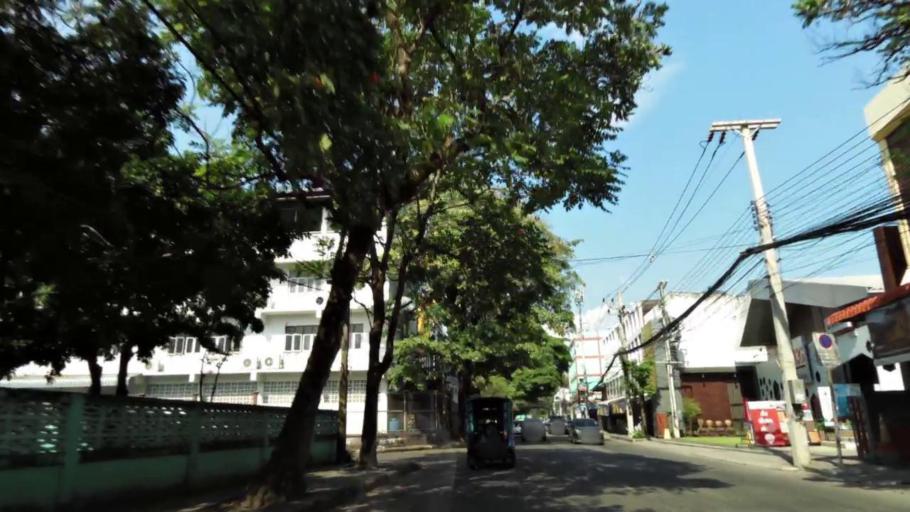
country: TH
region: Chiang Rai
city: Chiang Rai
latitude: 19.9101
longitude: 99.8328
